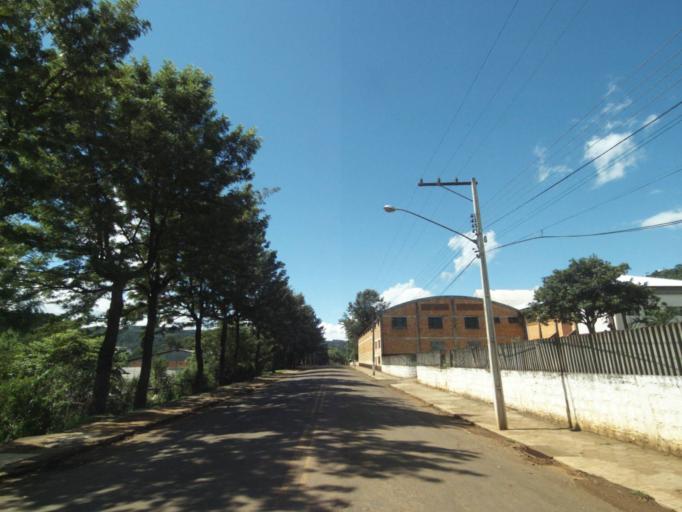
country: BR
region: Parana
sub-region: Uniao Da Vitoria
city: Uniao da Vitoria
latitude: -26.1640
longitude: -51.5531
